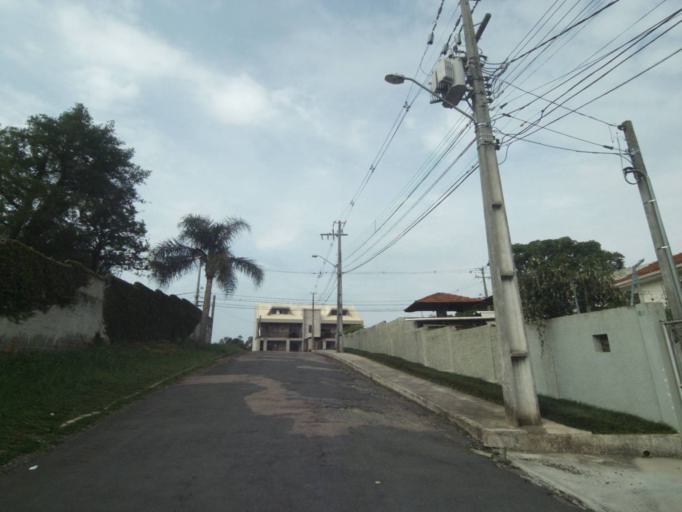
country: BR
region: Parana
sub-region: Curitiba
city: Curitiba
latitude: -25.4028
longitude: -49.3106
